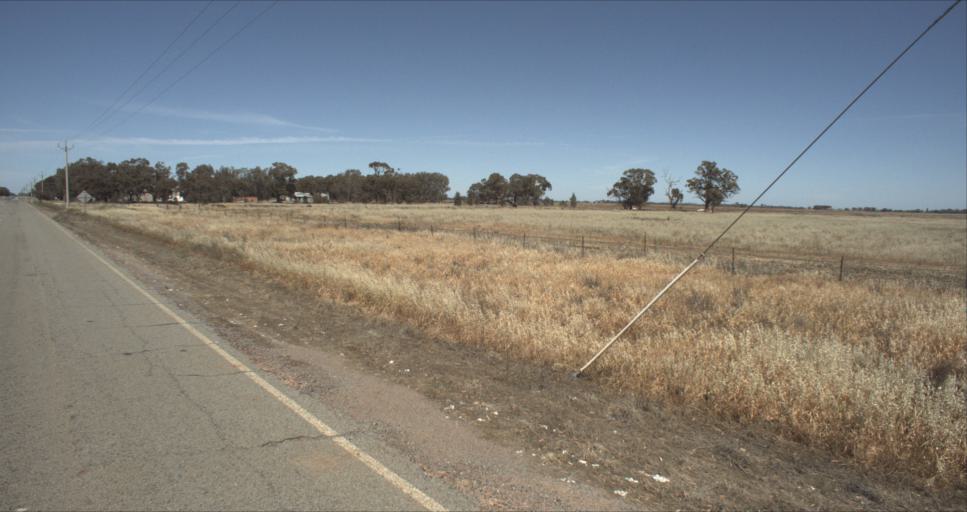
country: AU
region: New South Wales
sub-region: Leeton
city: Leeton
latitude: -34.4942
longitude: 146.2881
